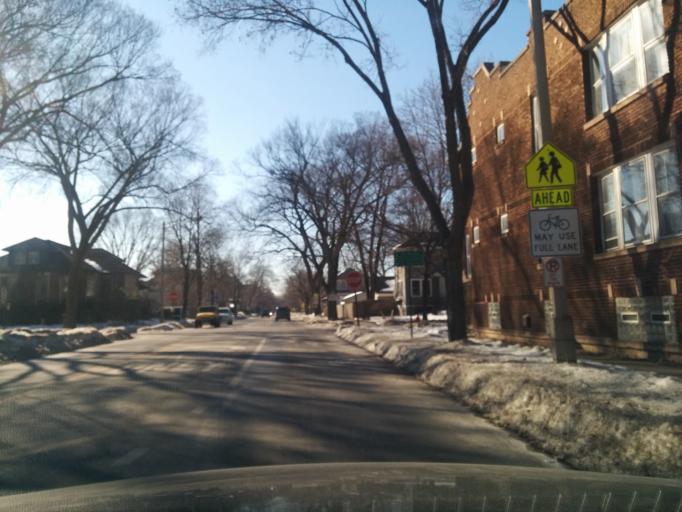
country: US
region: Illinois
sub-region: Cook County
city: Oak Park
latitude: 41.8762
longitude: -87.7887
